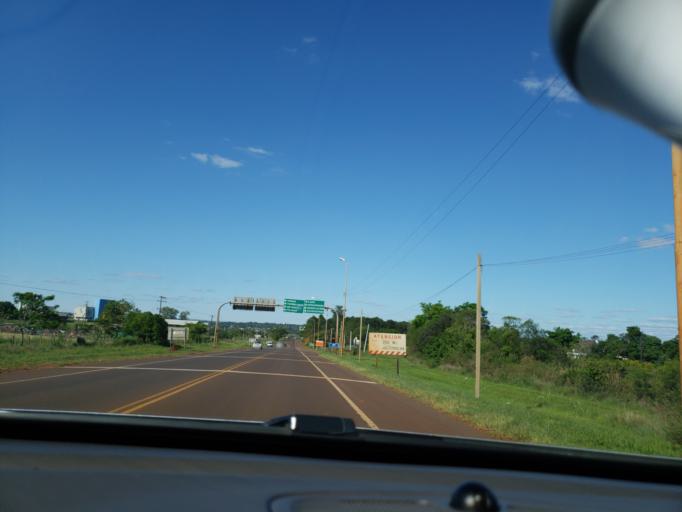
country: AR
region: Misiones
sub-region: Departamento de Capital
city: Posadas
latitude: -27.4033
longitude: -55.9686
